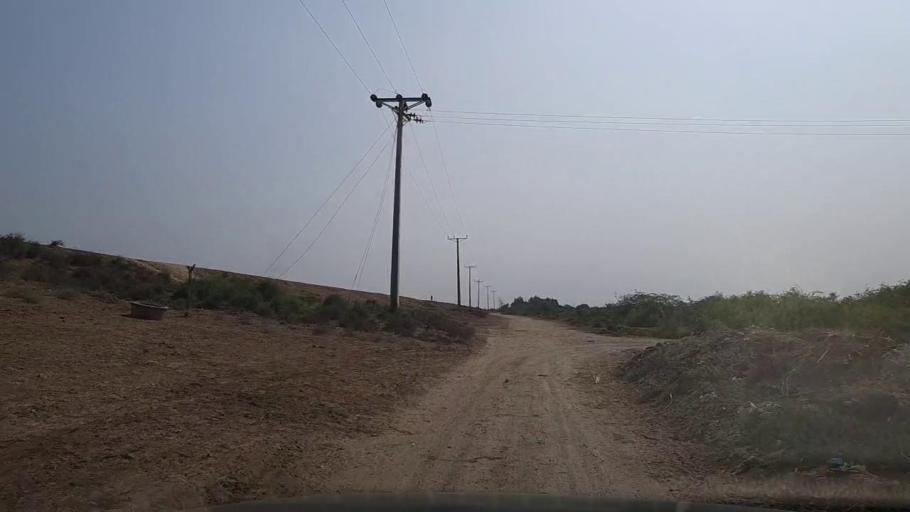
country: PK
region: Sindh
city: Chuhar Jamali
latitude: 24.5569
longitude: 67.9158
